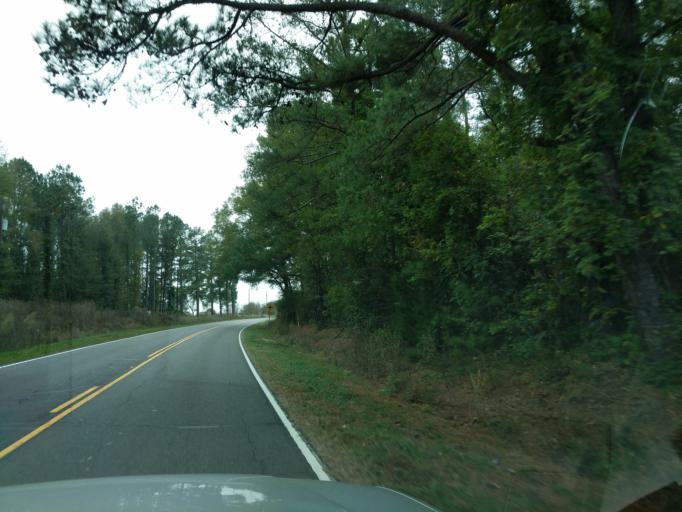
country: US
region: South Carolina
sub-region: Lexington County
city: Batesburg
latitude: 33.9236
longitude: -81.5847
